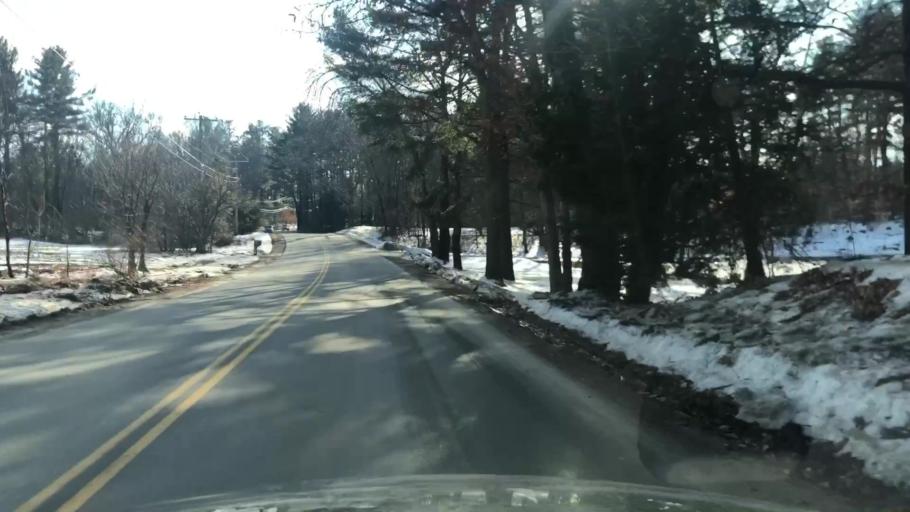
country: US
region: New Hampshire
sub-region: Hillsborough County
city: Wilton
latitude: 42.8488
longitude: -71.7010
